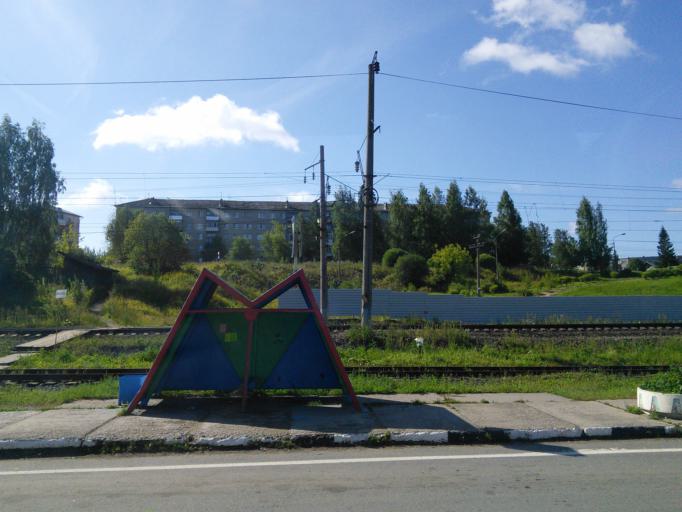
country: RU
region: Vologda
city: Sheksna
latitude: 59.2098
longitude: 38.5030
